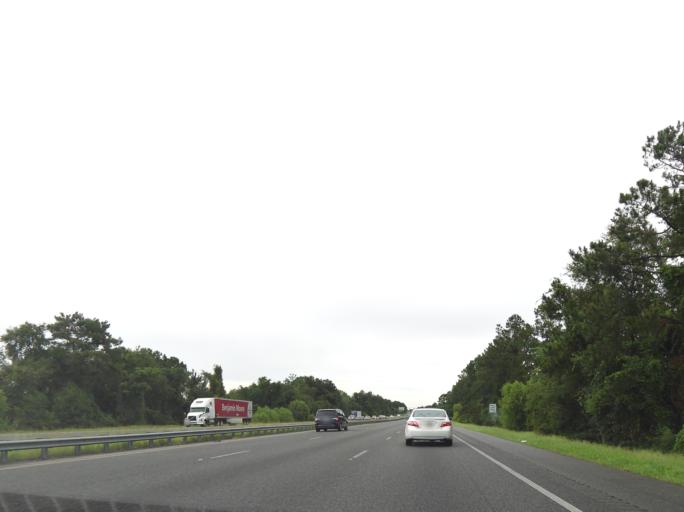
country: US
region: Georgia
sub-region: Lowndes County
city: Valdosta
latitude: 30.7888
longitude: -83.3008
